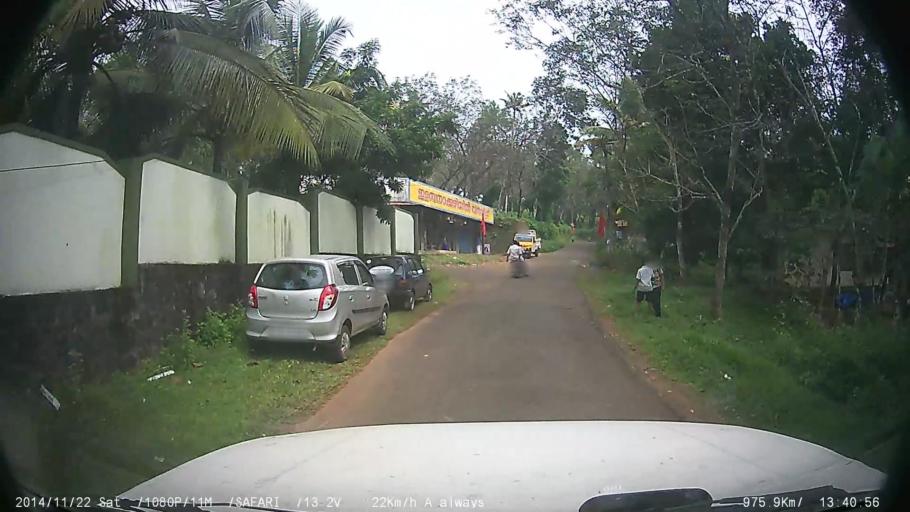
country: IN
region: Kerala
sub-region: Kottayam
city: Palackattumala
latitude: 9.7854
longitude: 76.5606
